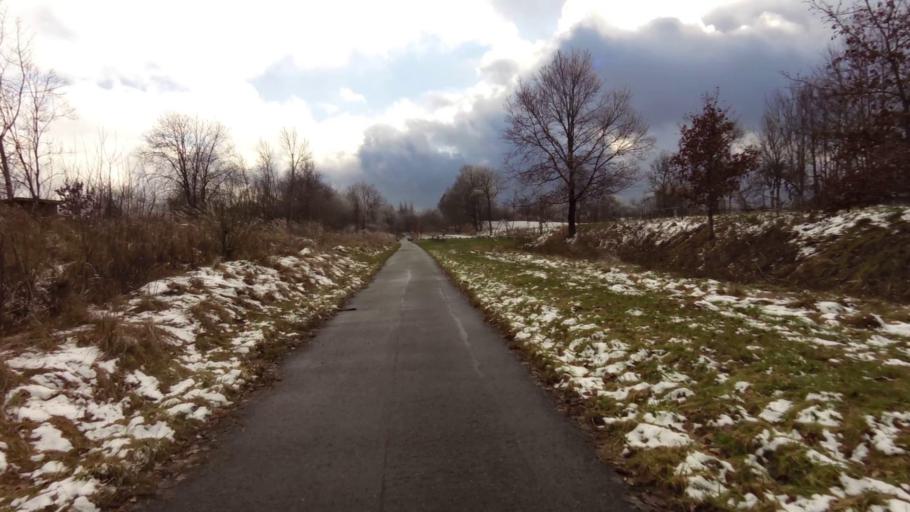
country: PL
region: West Pomeranian Voivodeship
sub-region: Powiat swidwinski
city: Polczyn-Zdroj
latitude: 53.7322
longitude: 16.0430
